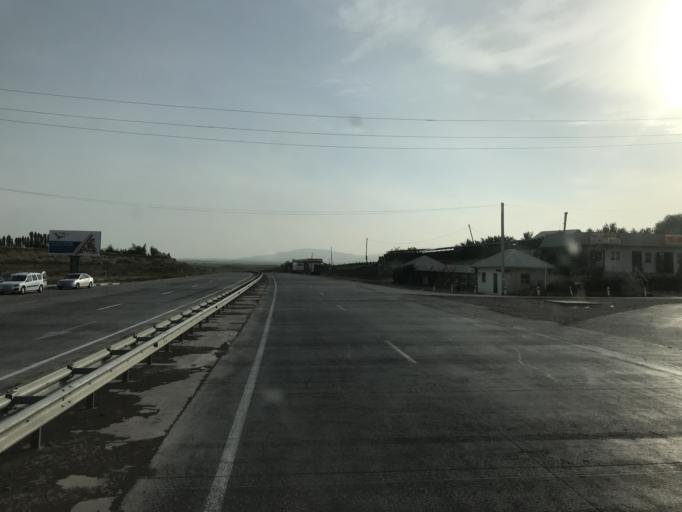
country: UZ
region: Toshkent
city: Qibray
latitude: 41.5266
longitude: 69.4002
